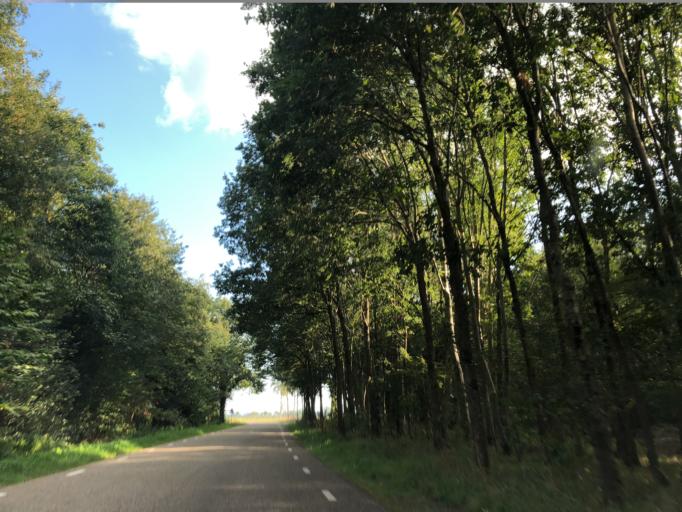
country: NL
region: Groningen
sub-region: Gemeente Vlagtwedde
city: Sellingen
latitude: 53.0054
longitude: 7.1846
